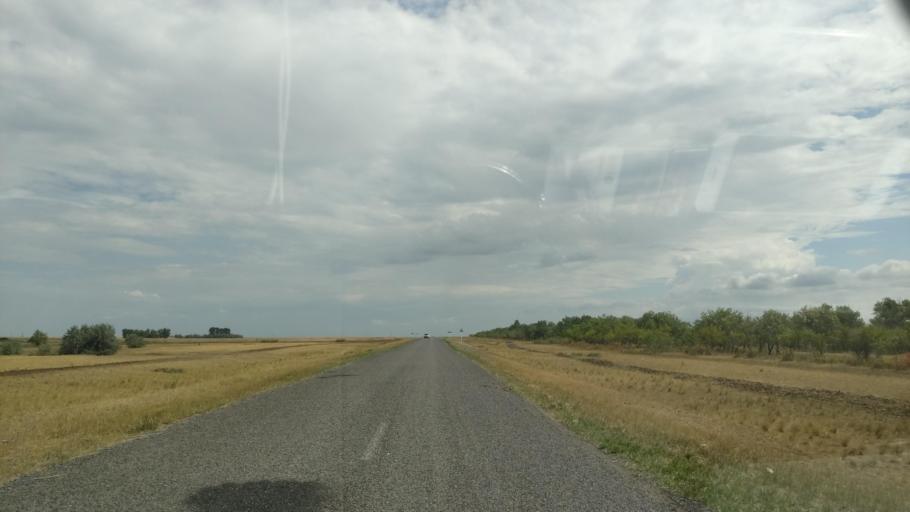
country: KZ
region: Pavlodar
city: Pavlodar
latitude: 52.6417
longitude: 77.0222
